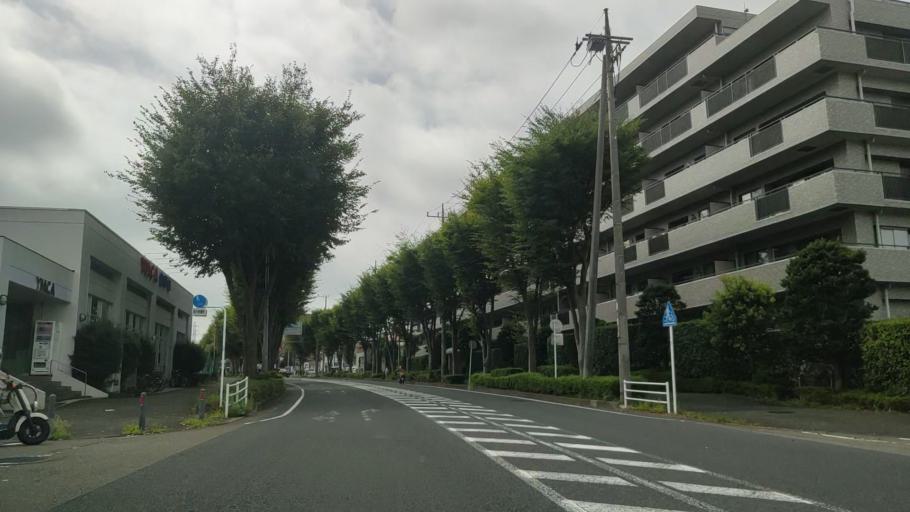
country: JP
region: Kanagawa
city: Fujisawa
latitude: 35.4192
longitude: 139.5235
